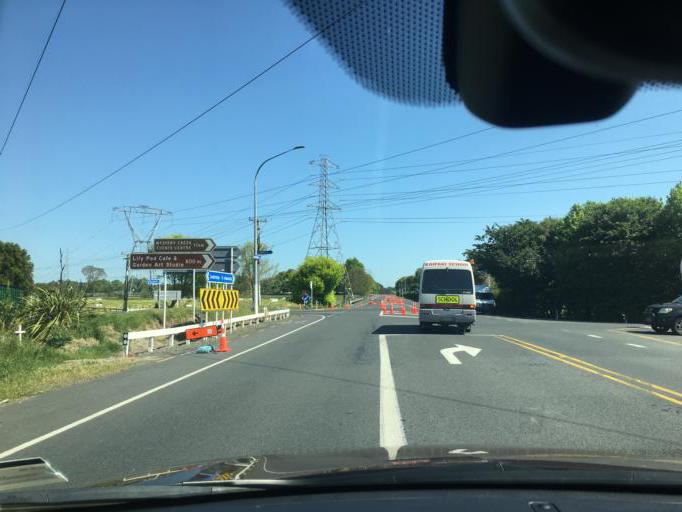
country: NZ
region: Waikato
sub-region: Waipa District
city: Cambridge
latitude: -37.9062
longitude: 175.4511
